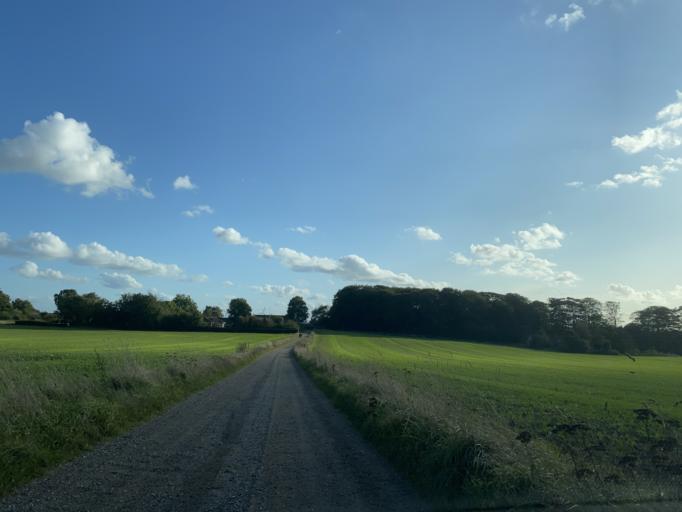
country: DK
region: Central Jutland
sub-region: Skanderborg Kommune
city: Ry
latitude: 56.1538
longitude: 9.7830
